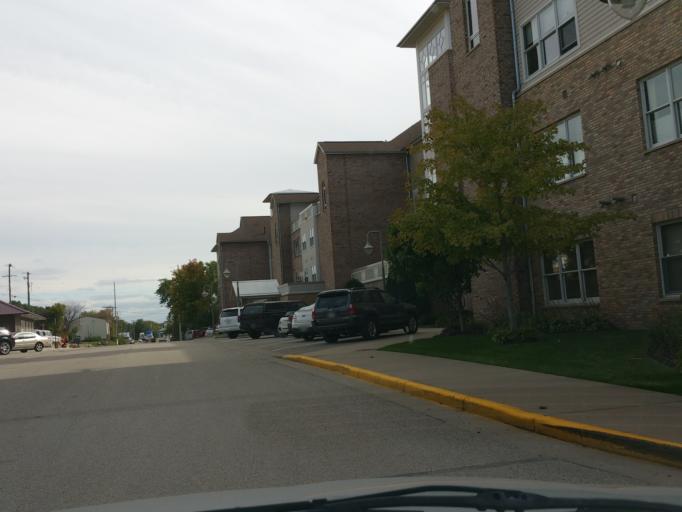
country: US
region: Wisconsin
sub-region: Pierce County
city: Prescott
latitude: 44.7474
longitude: -92.8009
